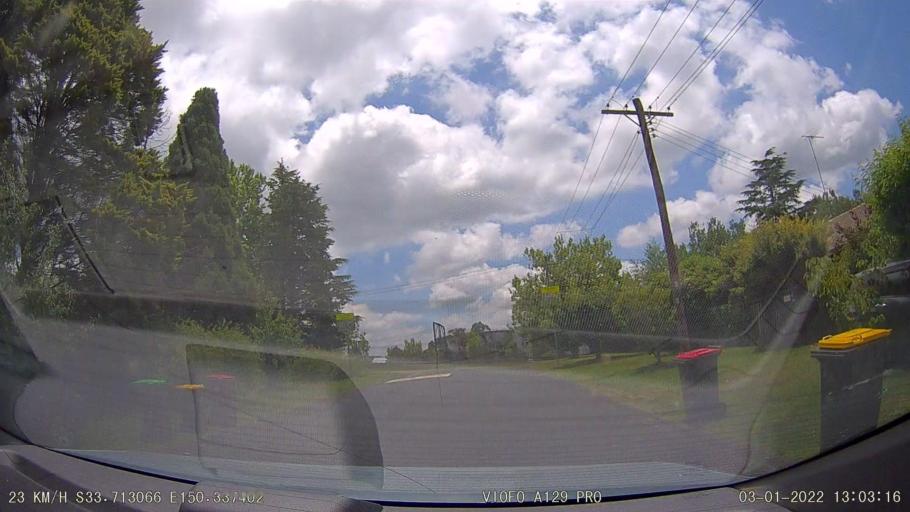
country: AU
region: New South Wales
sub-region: Blue Mountains Municipality
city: Leura
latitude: -33.7131
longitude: 150.3374
